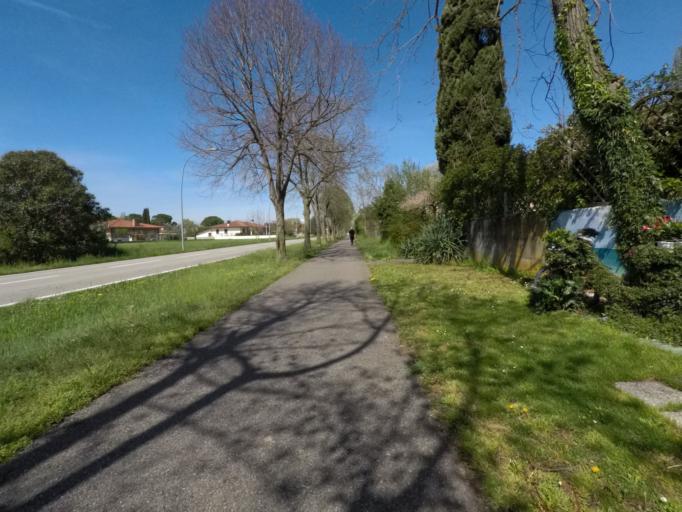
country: IT
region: Friuli Venezia Giulia
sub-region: Provincia di Udine
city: Codroipo
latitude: 45.9545
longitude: 12.9972
